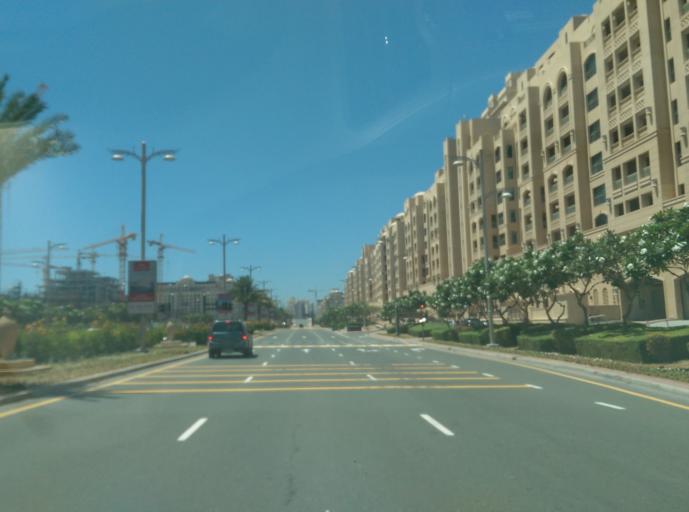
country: AE
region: Dubai
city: Dubai
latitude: 25.1052
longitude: 55.1488
